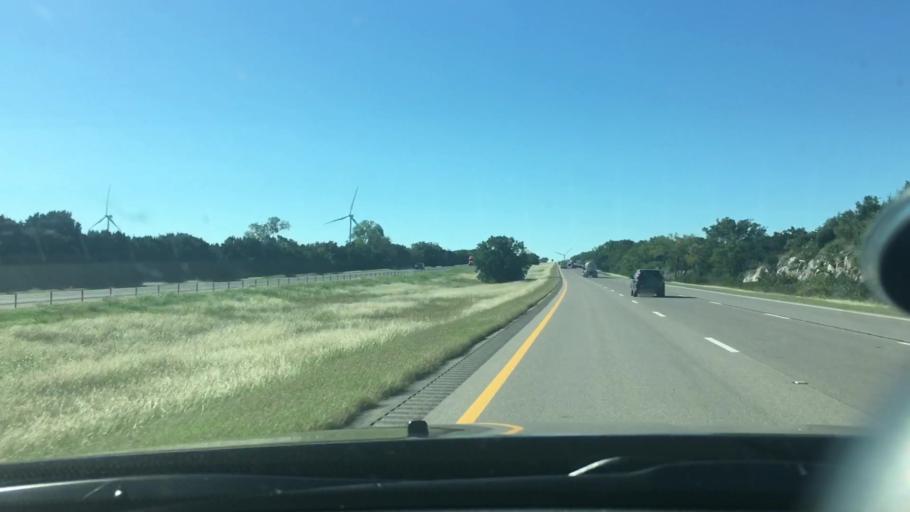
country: US
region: Oklahoma
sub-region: Murray County
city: Davis
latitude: 34.4157
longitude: -97.1379
